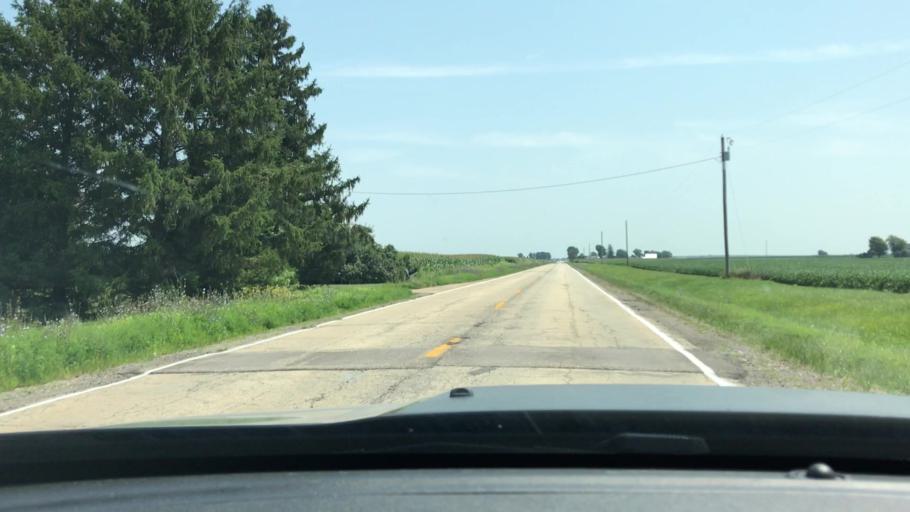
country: US
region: Illinois
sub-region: LaSalle County
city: Ottawa
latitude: 41.4702
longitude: -88.8575
